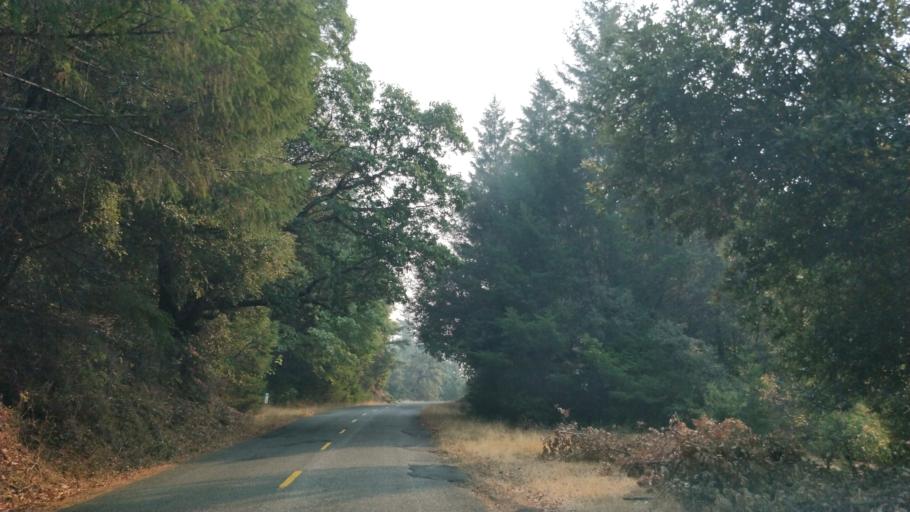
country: US
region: California
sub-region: Humboldt County
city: Rio Dell
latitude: 40.2563
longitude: -124.1193
